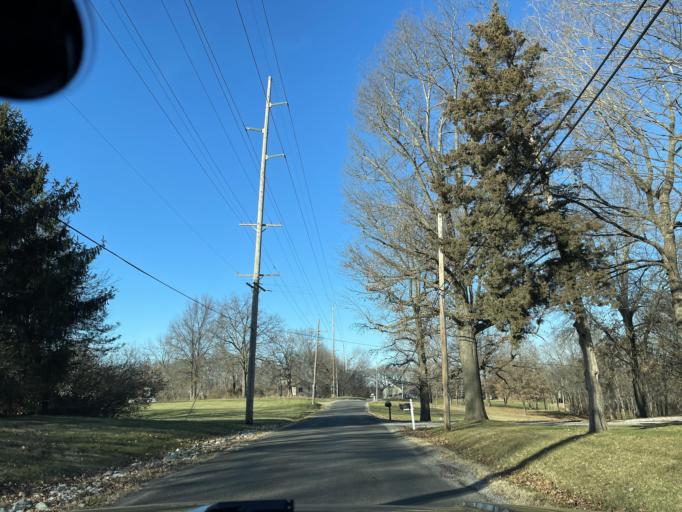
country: US
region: Illinois
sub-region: Sangamon County
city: Leland Grove
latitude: 39.8071
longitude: -89.7157
